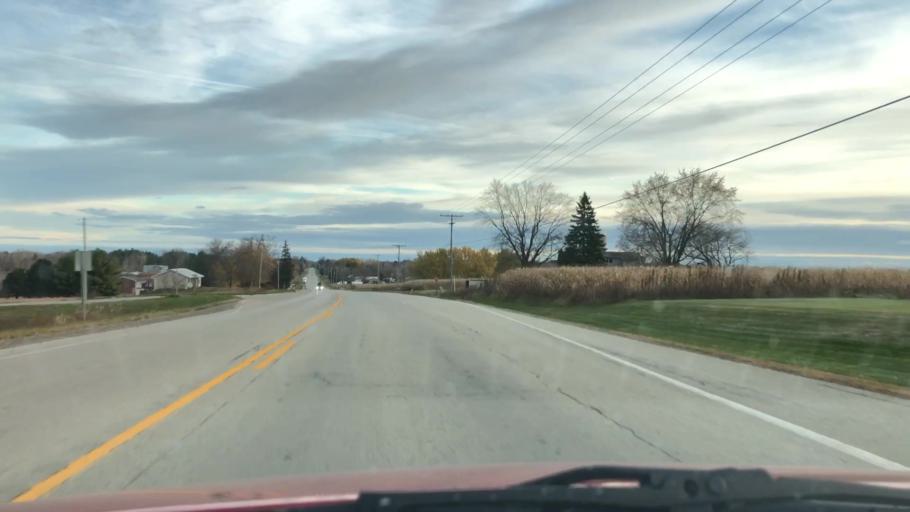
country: US
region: Wisconsin
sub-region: Brown County
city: Oneida
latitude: 44.4331
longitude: -88.2364
